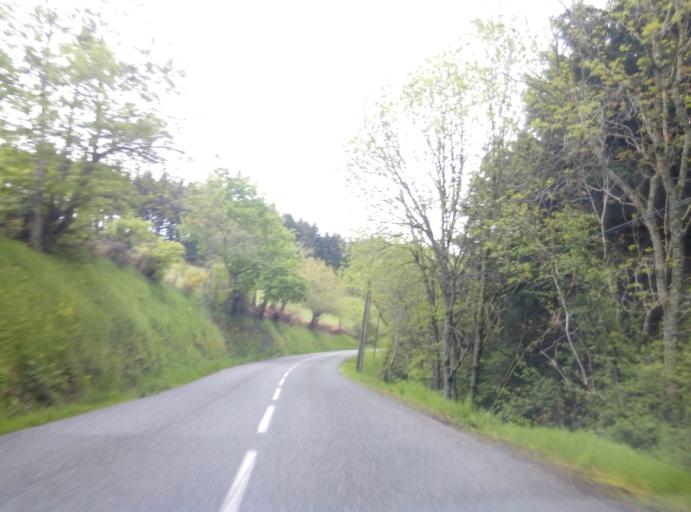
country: FR
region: Rhone-Alpes
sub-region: Departement du Rhone
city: Tarare
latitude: 45.9352
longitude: 4.4233
